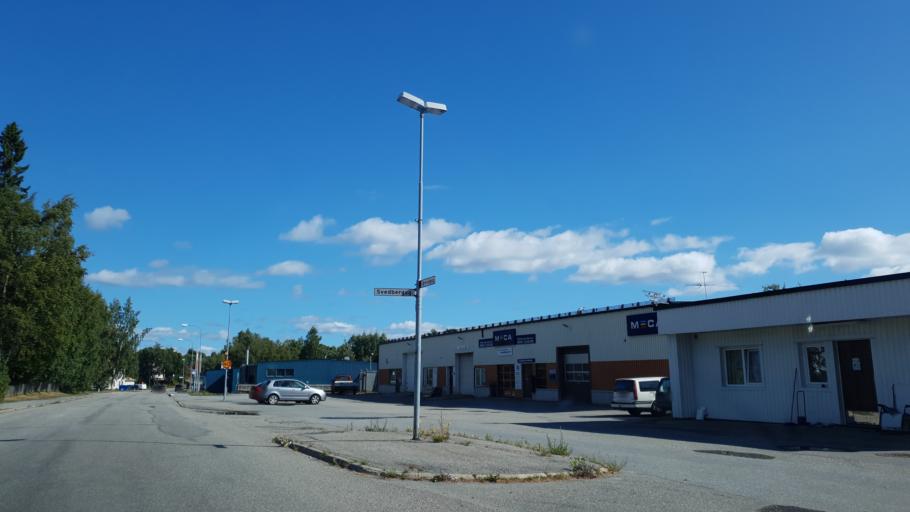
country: SE
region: Vaesterbotten
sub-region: Umea Kommun
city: Holmsund
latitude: 63.7098
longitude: 20.3700
